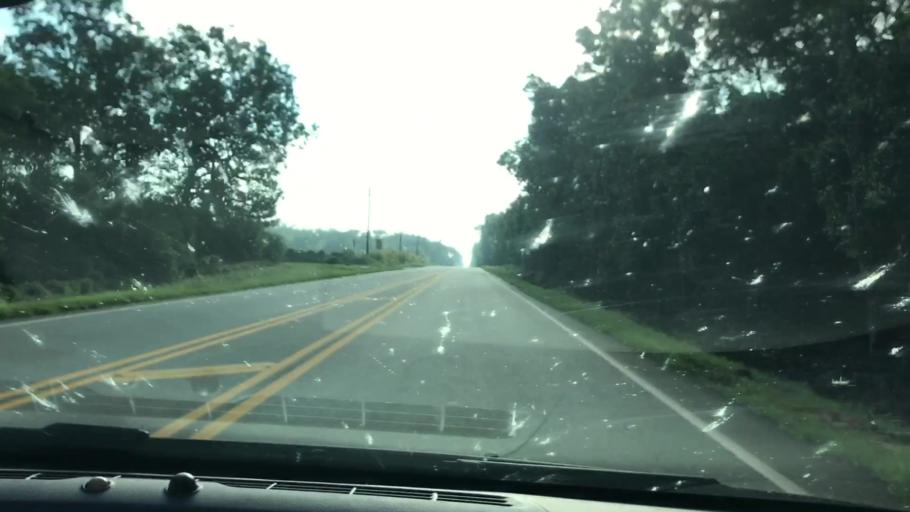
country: US
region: Georgia
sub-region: Terrell County
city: Dawson
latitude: 31.7703
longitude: -84.4981
